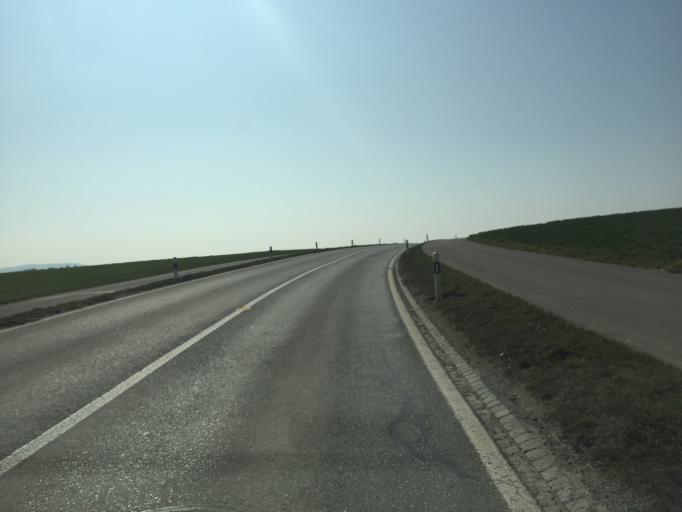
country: CH
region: Thurgau
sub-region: Frauenfeld District
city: Huttwilen
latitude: 47.5946
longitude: 8.8923
